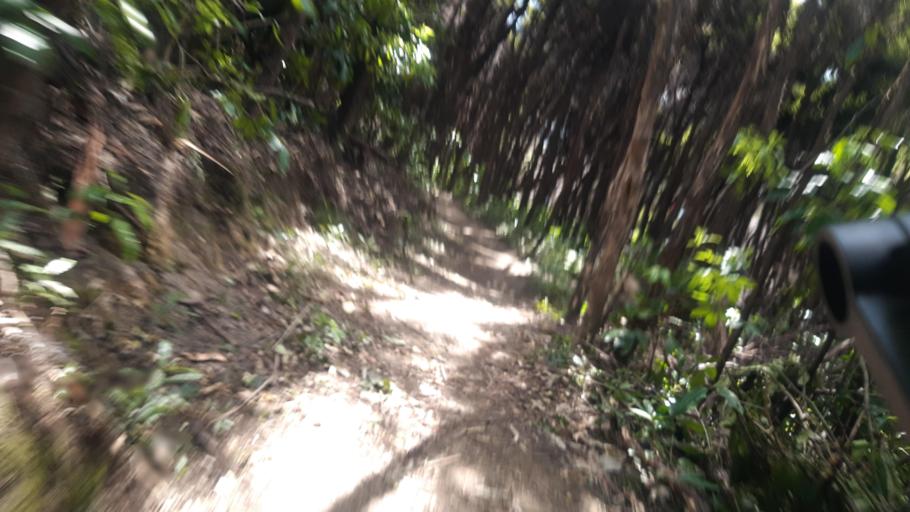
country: NZ
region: Marlborough
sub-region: Marlborough District
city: Picton
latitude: -41.2549
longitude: 174.0378
